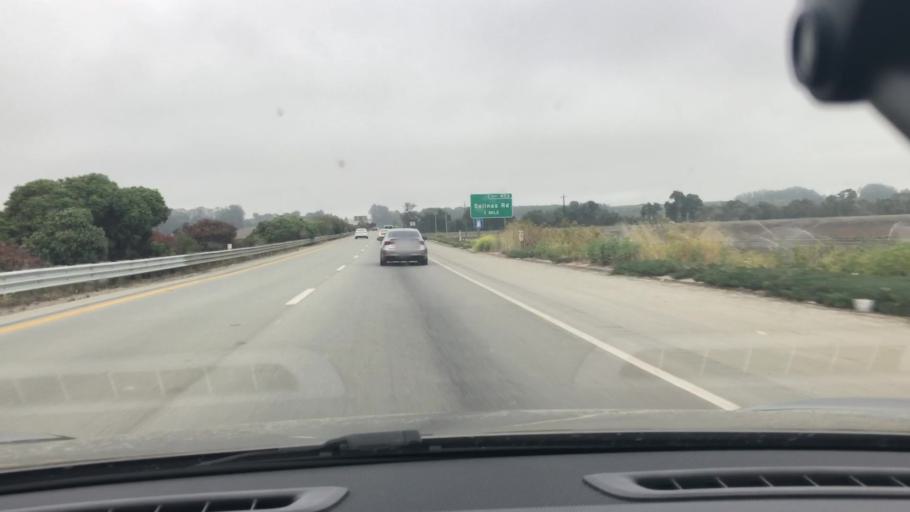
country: US
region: California
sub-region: Santa Cruz County
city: Watsonville
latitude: 36.8892
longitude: -121.7733
